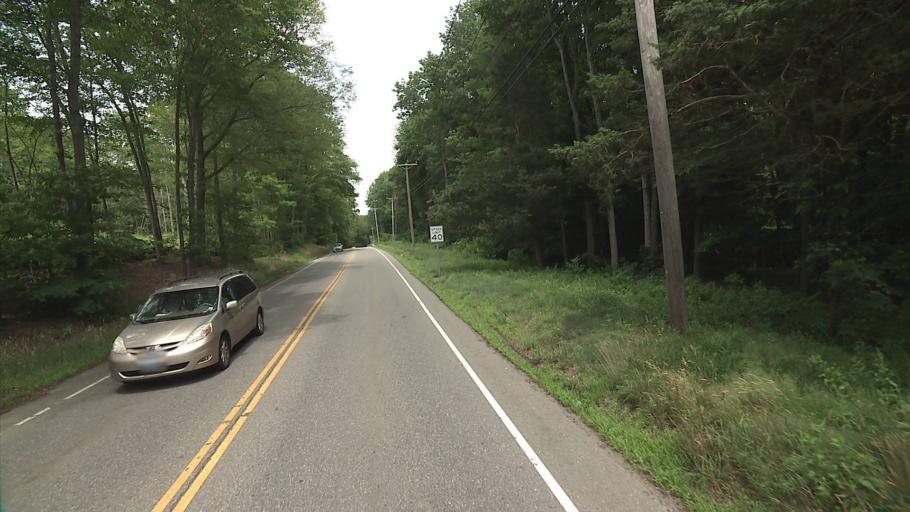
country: US
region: Connecticut
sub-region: New London County
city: Preston City
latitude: 41.5132
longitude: -71.9826
